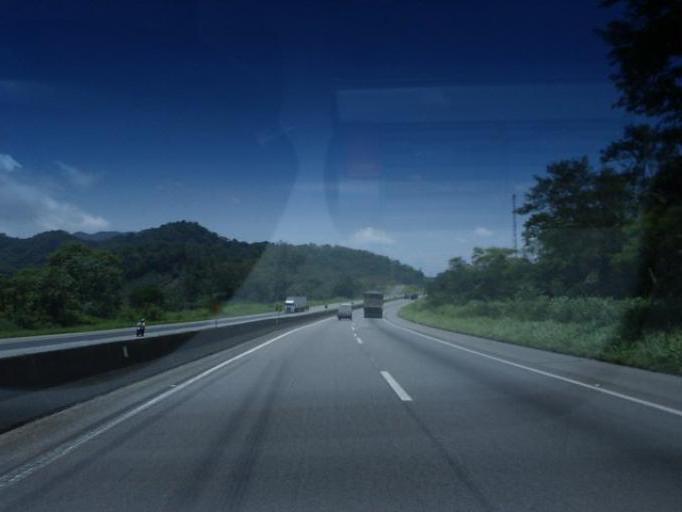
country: BR
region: Sao Paulo
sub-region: Miracatu
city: Miracatu
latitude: -24.3206
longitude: -47.5344
